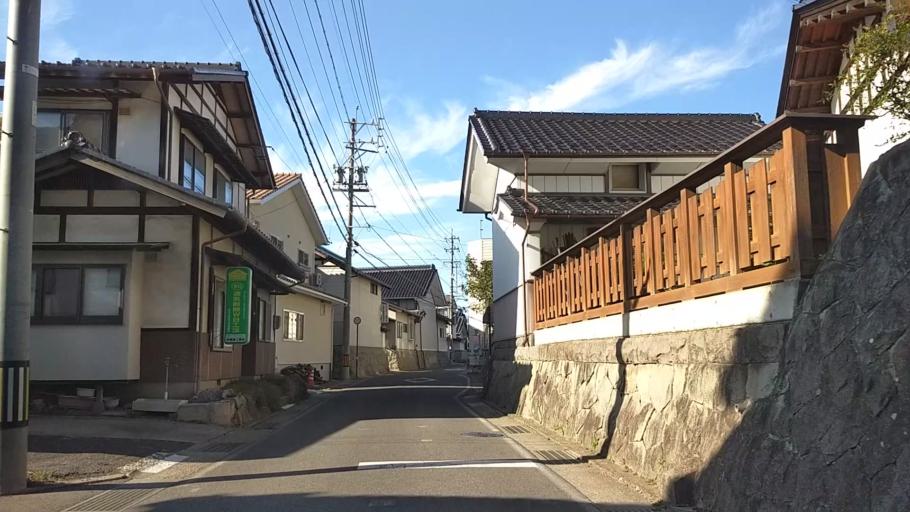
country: JP
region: Nagano
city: Nagano-shi
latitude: 36.5523
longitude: 138.1563
